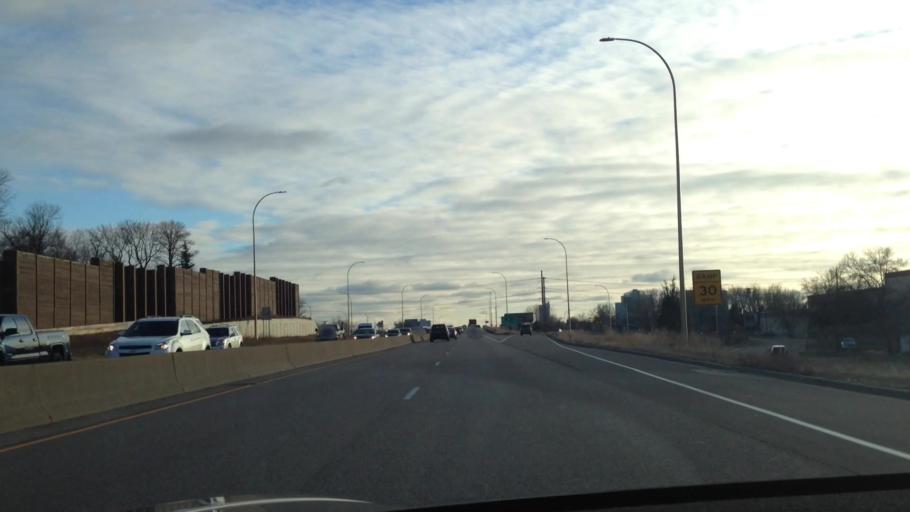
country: US
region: Minnesota
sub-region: Hennepin County
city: New Hope
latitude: 44.9963
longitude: -93.4010
